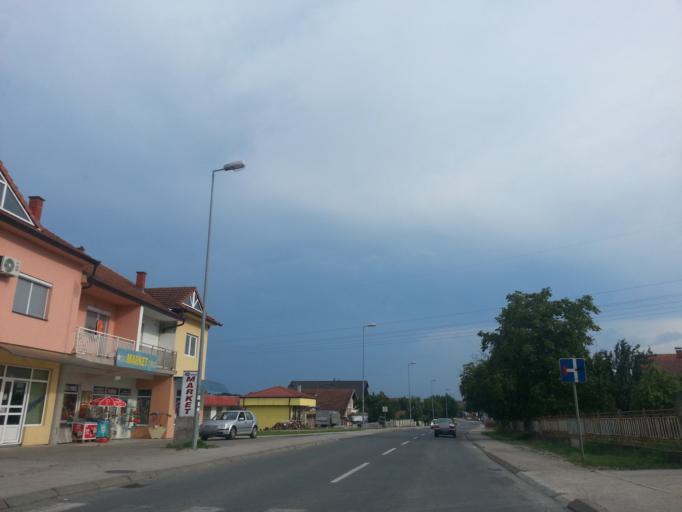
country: BA
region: Brcko
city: Brcko
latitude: 44.8557
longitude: 18.8137
